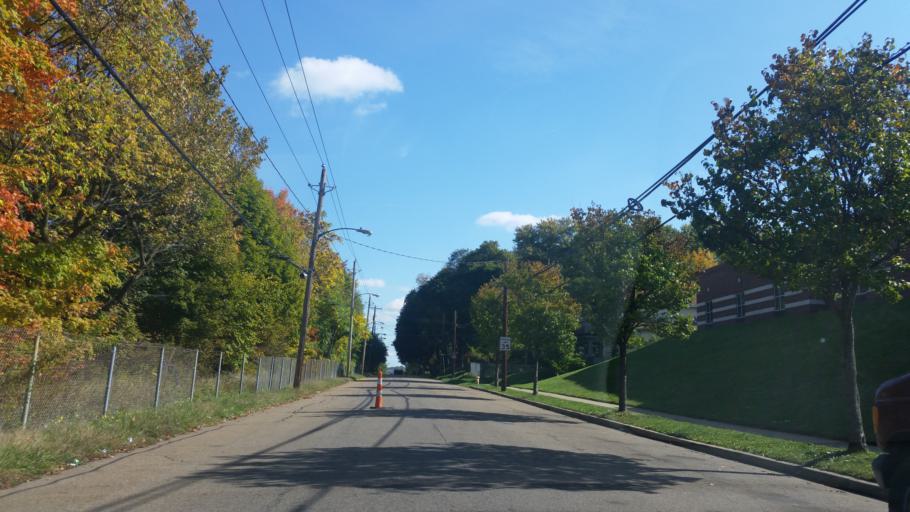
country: US
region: Ohio
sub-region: Summit County
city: Akron
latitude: 41.0617
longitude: -81.5343
